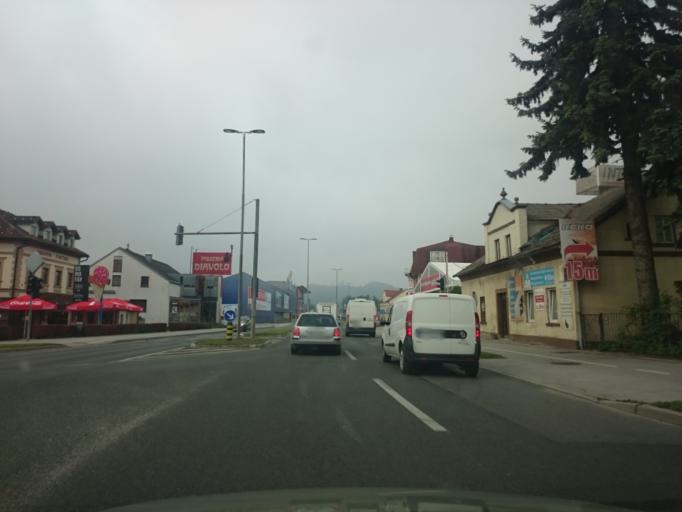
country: SI
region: Celje
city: Celje
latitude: 46.2433
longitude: 15.2772
